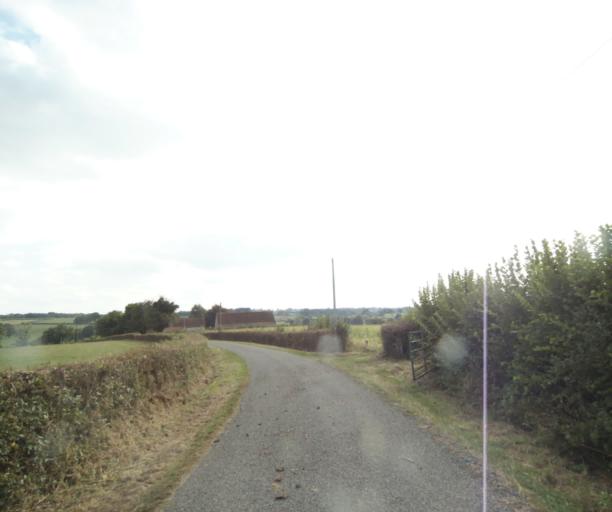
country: FR
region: Bourgogne
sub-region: Departement de Saone-et-Loire
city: Palinges
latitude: 46.5002
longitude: 4.2485
